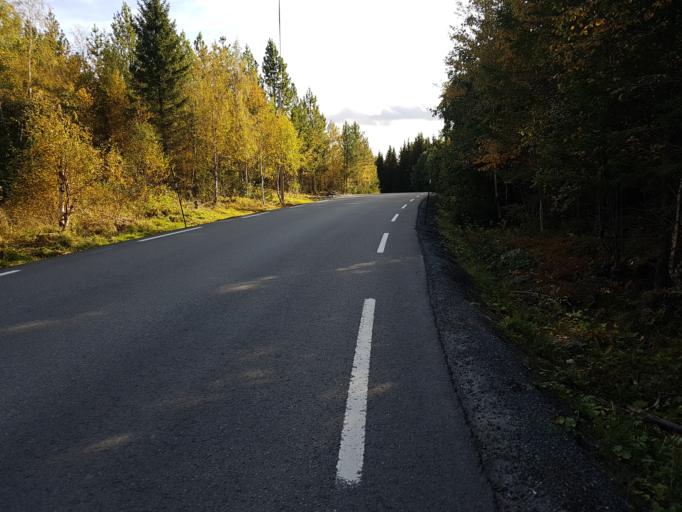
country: NO
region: Sor-Trondelag
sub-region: Malvik
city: Malvik
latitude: 63.3701
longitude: 10.6159
